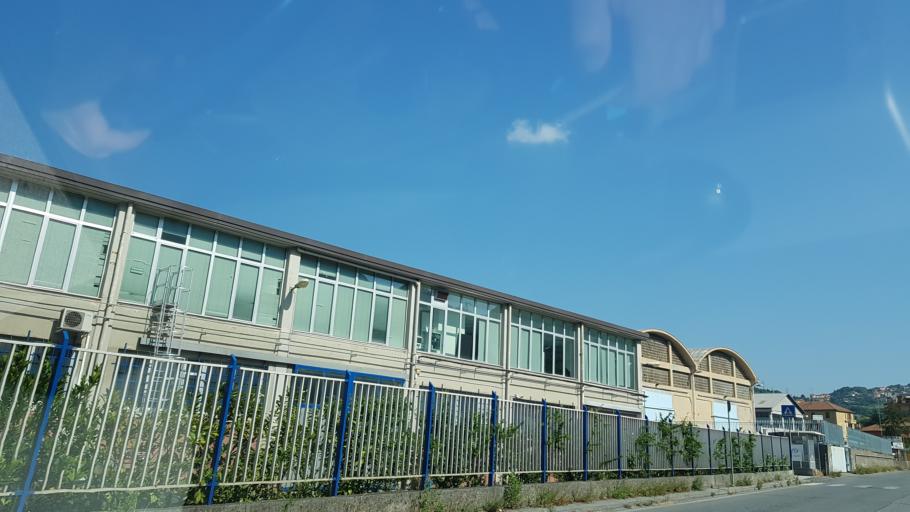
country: IT
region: Liguria
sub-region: Provincia di Genova
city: Manesseno
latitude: 44.4878
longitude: 8.9215
